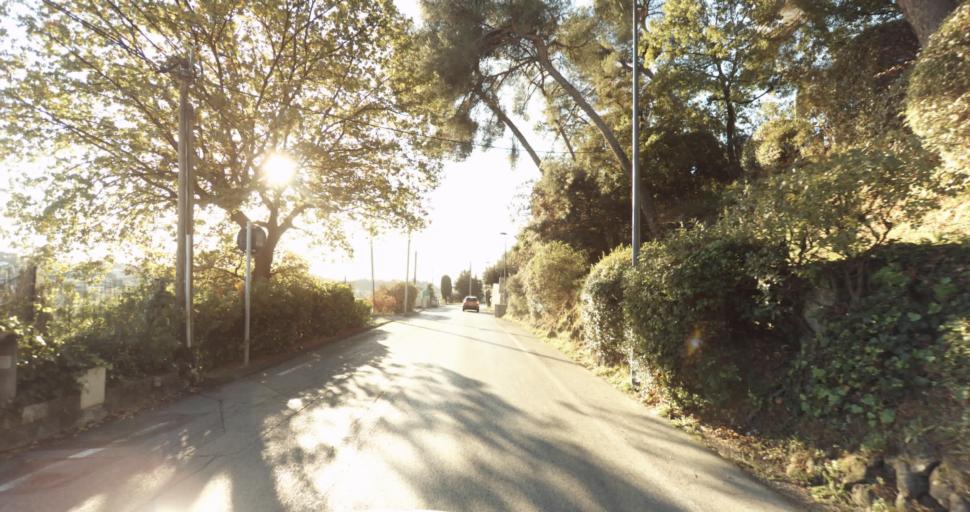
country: FR
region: Provence-Alpes-Cote d'Azur
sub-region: Departement des Alpes-Maritimes
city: Vence
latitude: 43.7176
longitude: 7.1243
